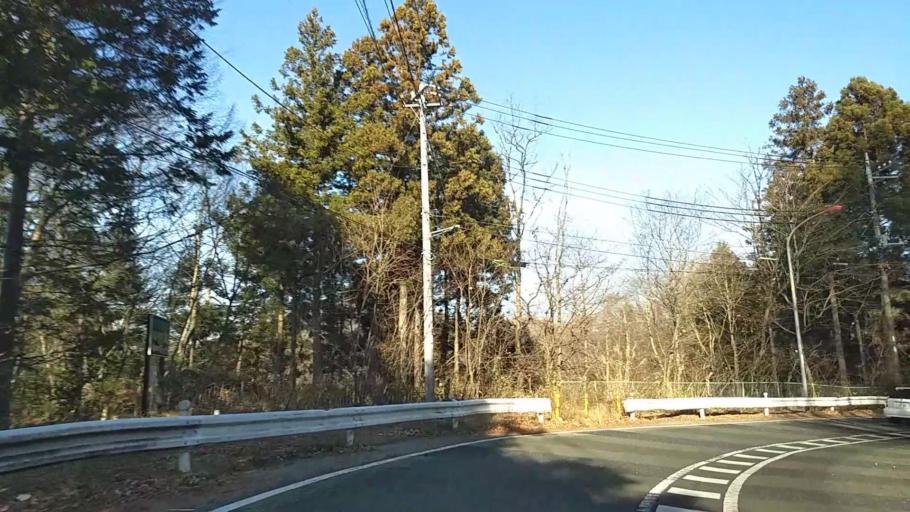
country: JP
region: Yamanashi
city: Uenohara
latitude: 35.5503
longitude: 139.1531
